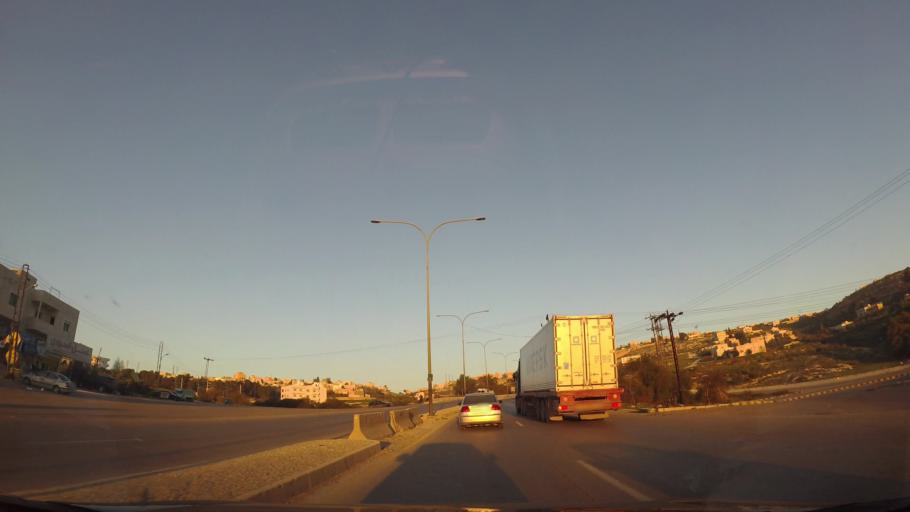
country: JO
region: Amman
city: Umm as Summaq
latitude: 31.8607
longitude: 35.8063
